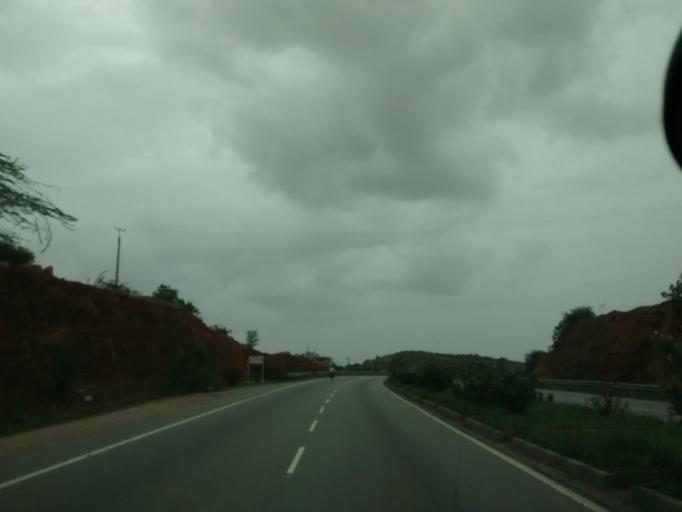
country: IN
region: Andhra Pradesh
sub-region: Kurnool
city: Ramapuram
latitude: 15.2167
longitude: 77.7225
